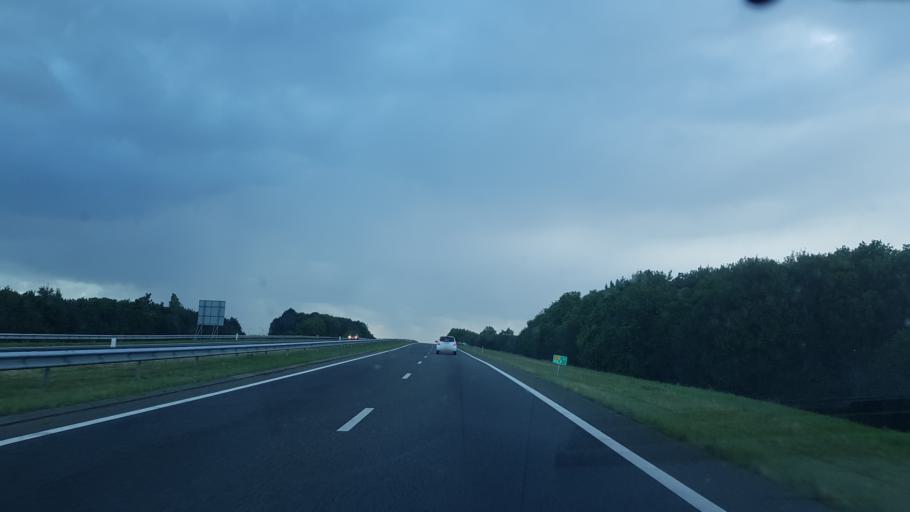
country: NL
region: Friesland
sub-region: Gemeente Smallingerland
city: Opeinde
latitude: 53.1458
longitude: 6.0268
